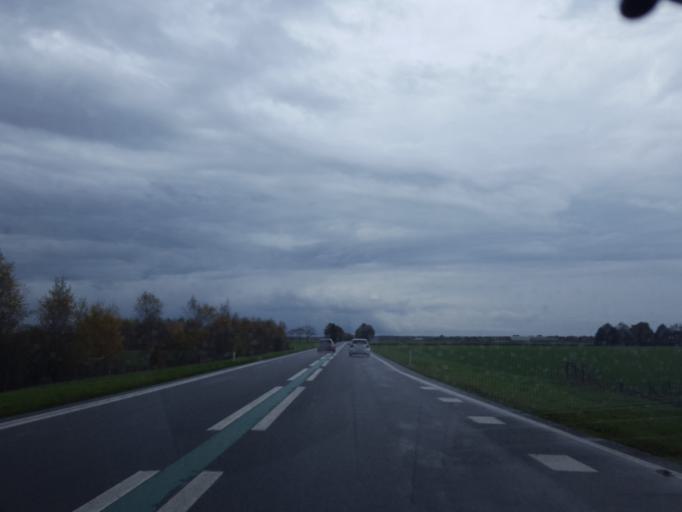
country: NL
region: Drenthe
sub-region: Gemeente Hoogeveen
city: Hoogeveen
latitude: 52.8300
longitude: 6.6117
